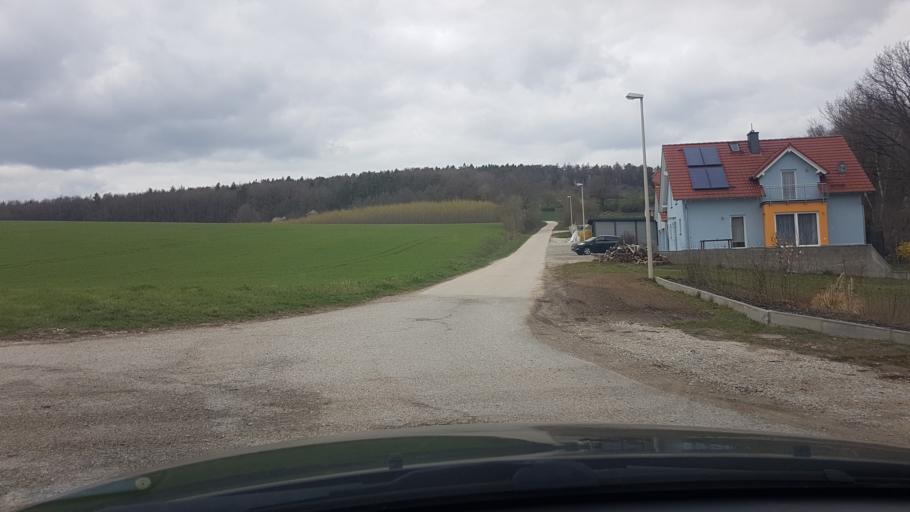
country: DE
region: Bavaria
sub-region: Upper Franconia
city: Pettstadt
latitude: 49.8023
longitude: 10.9207
